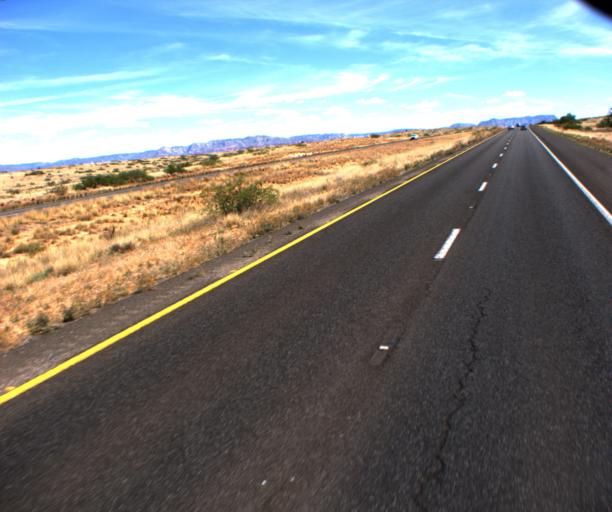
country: US
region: Arizona
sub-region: Yavapai County
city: Cottonwood
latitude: 34.7498
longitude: -111.9615
